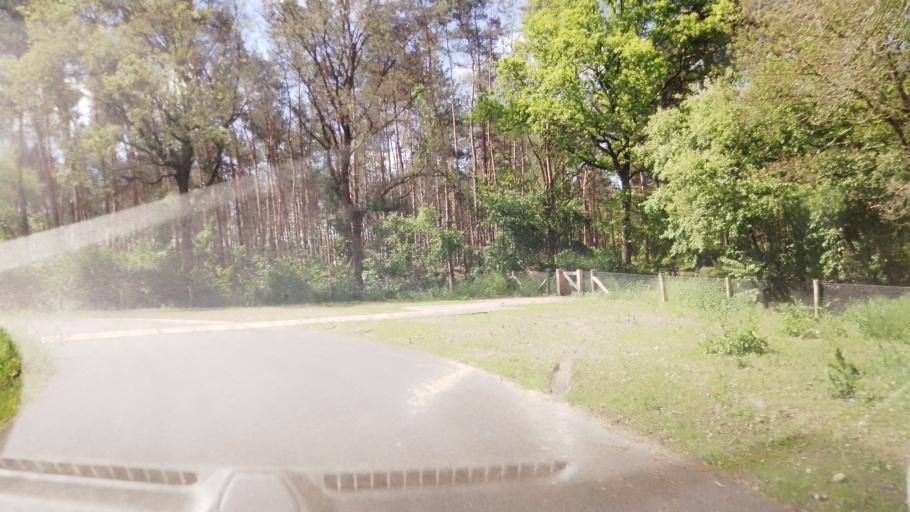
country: NL
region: Limburg
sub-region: Gemeente Venlo
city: Venlo
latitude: 51.4062
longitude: 6.1200
